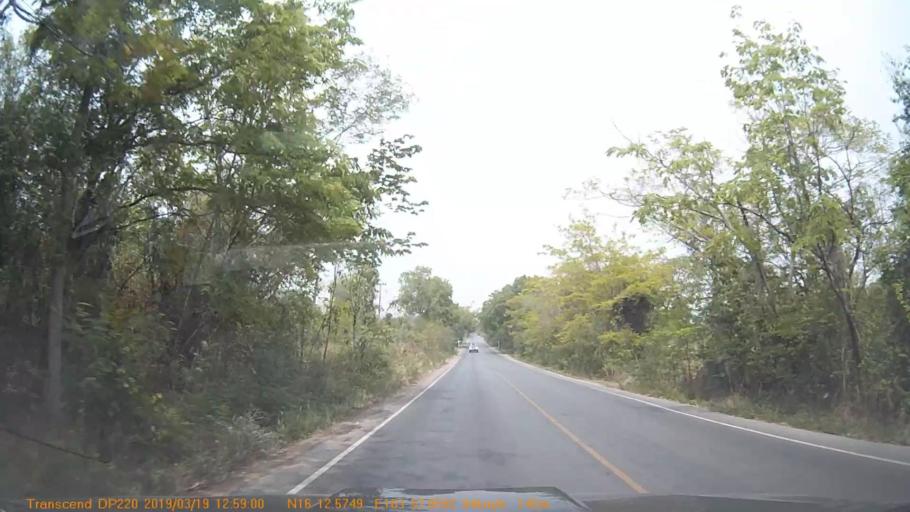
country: TH
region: Roi Et
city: Waeng
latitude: 16.2099
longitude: 103.9511
